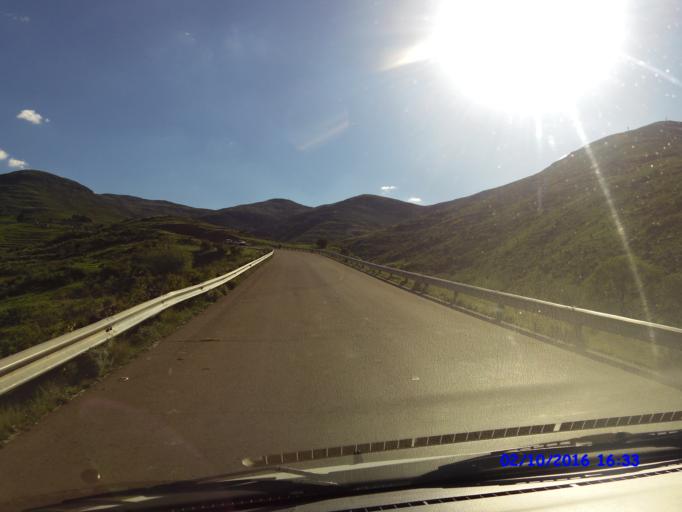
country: LS
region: Maseru
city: Nako
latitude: -29.4881
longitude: 28.0655
